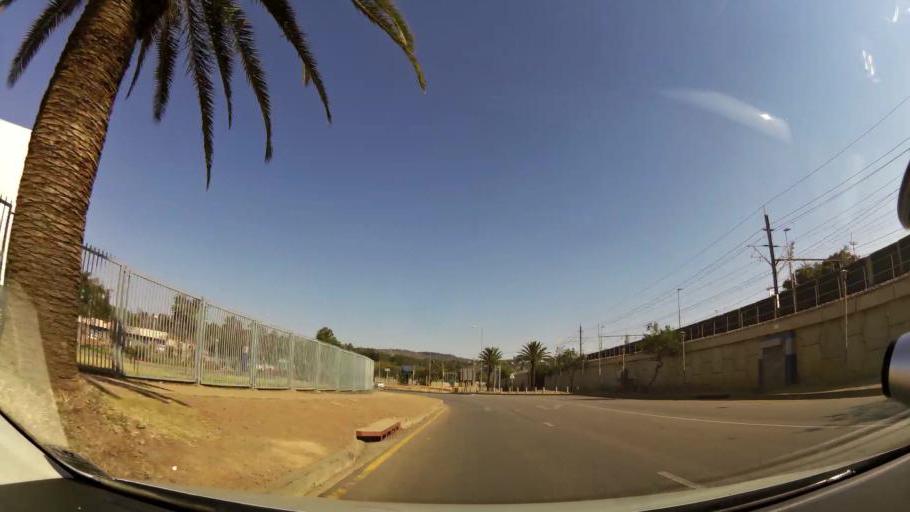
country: ZA
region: Gauteng
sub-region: City of Tshwane Metropolitan Municipality
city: Pretoria
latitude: -25.7552
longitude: 28.2255
